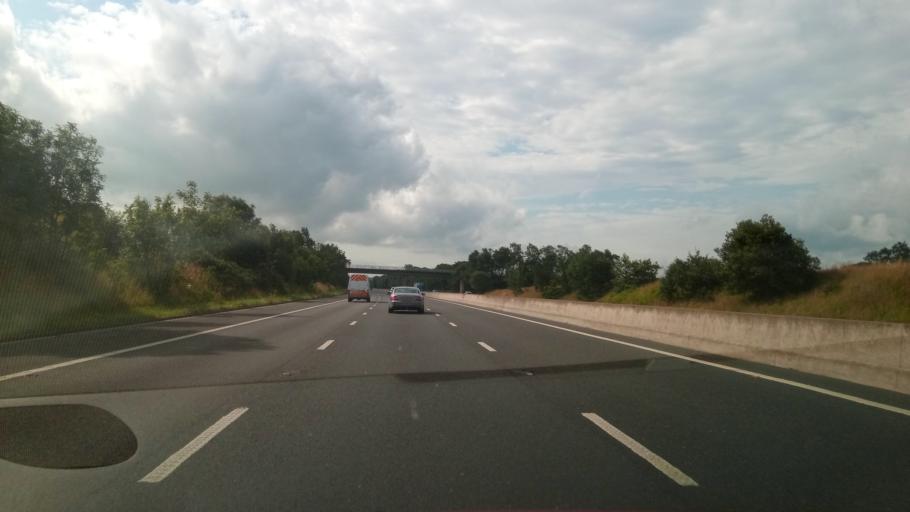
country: GB
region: England
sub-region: Cumbria
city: Scotby
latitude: 54.8280
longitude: -2.8894
